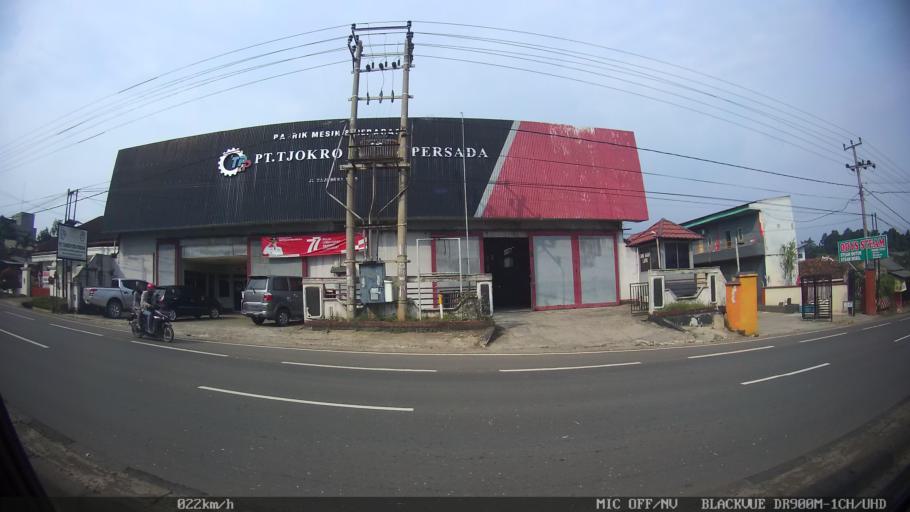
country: ID
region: Lampung
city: Kedaton
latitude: -5.3575
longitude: 105.2229
